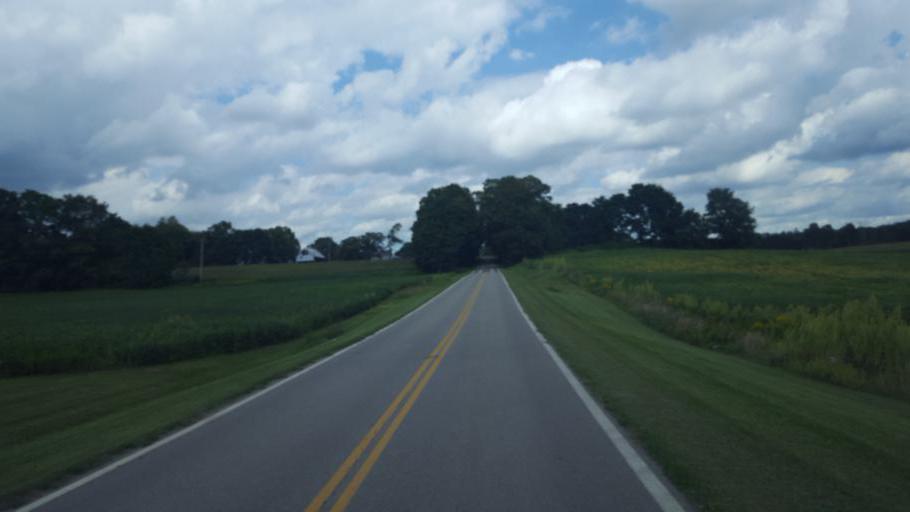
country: US
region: Ohio
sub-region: Huron County
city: Norwalk
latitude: 41.1629
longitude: -82.6325
